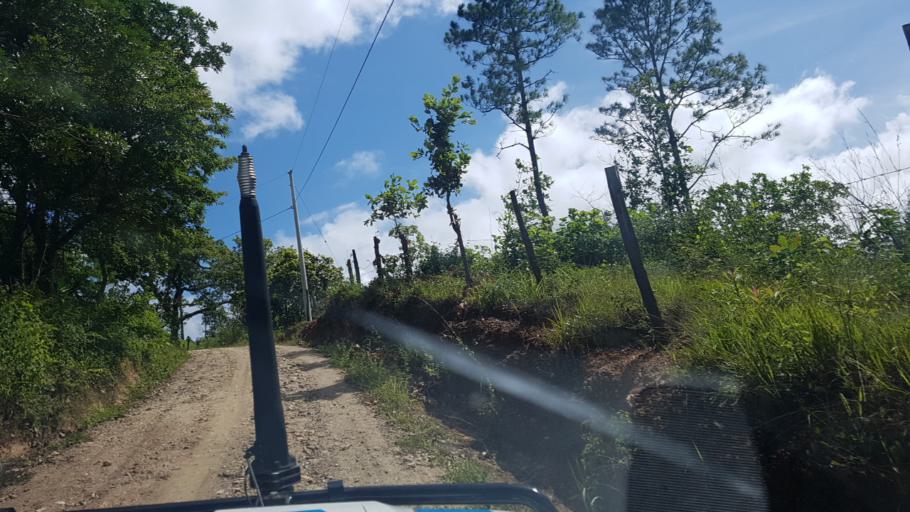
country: NI
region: Nueva Segovia
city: Ciudad Antigua
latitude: 13.6451
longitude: -86.2714
